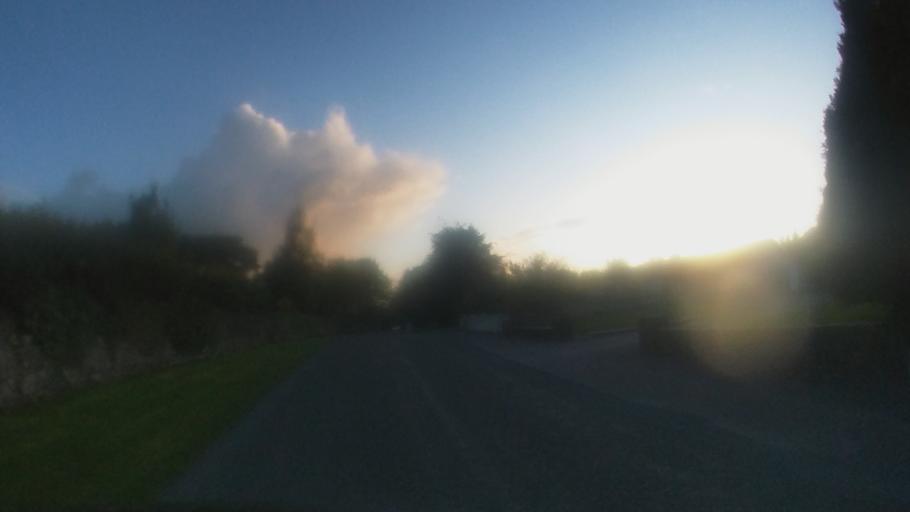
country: IE
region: Leinster
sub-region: An Iarmhi
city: Athlone
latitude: 53.4256
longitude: -7.8799
